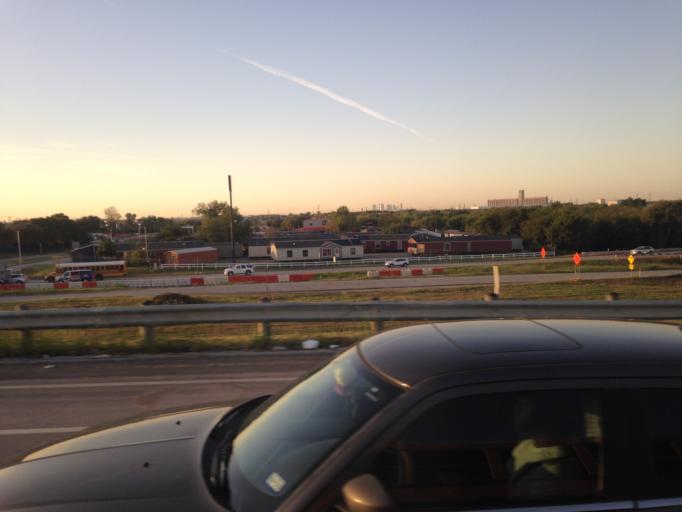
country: US
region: Texas
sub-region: Tarrant County
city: Blue Mound
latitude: 32.8395
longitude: -97.3222
